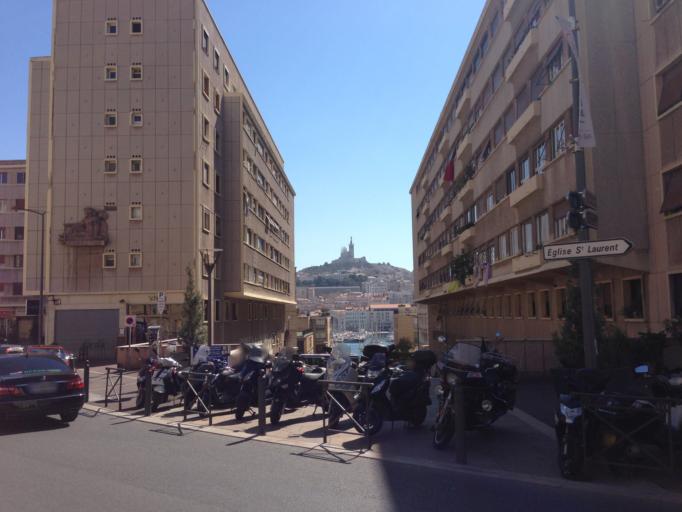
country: FR
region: Provence-Alpes-Cote d'Azur
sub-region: Departement des Bouches-du-Rhone
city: Marseille 02
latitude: 43.2973
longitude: 5.3657
